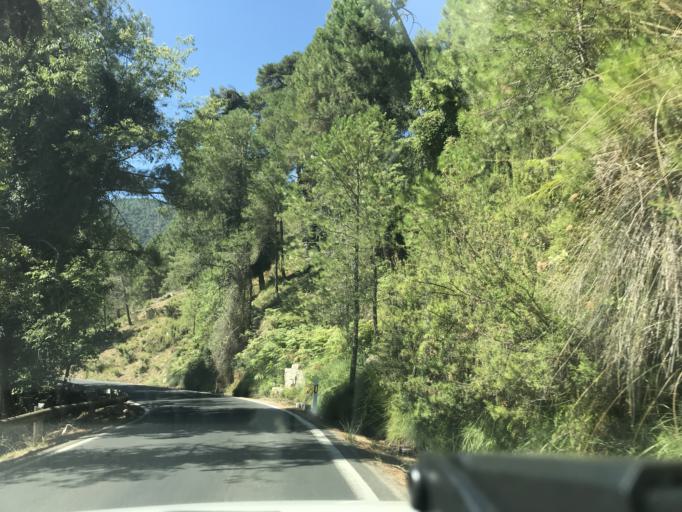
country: ES
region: Andalusia
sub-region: Provincia de Jaen
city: La Iruela
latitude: 37.9220
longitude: -2.9529
